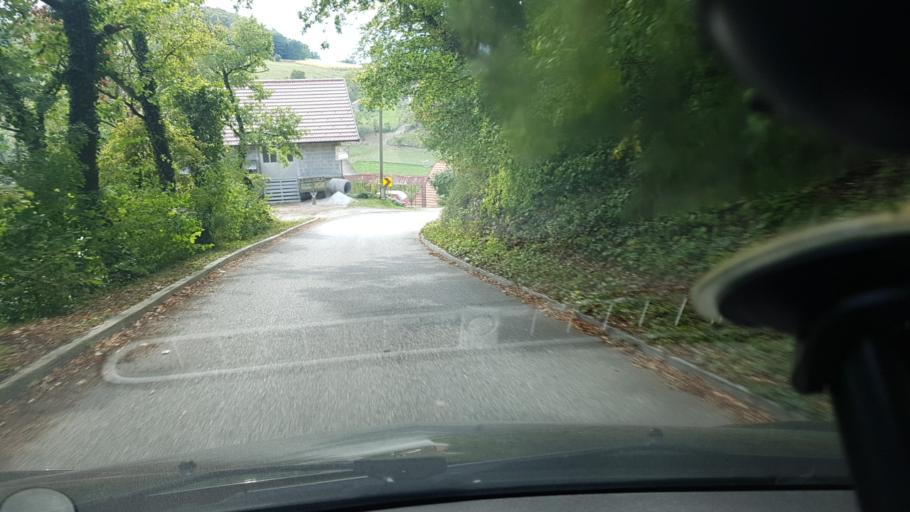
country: HR
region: Krapinsko-Zagorska
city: Radoboj
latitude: 46.1723
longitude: 15.9457
